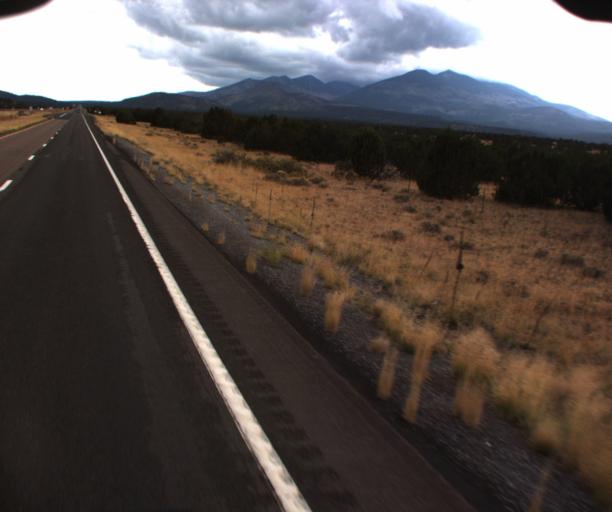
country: US
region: Arizona
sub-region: Coconino County
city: Flagstaff
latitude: 35.4306
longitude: -111.5685
